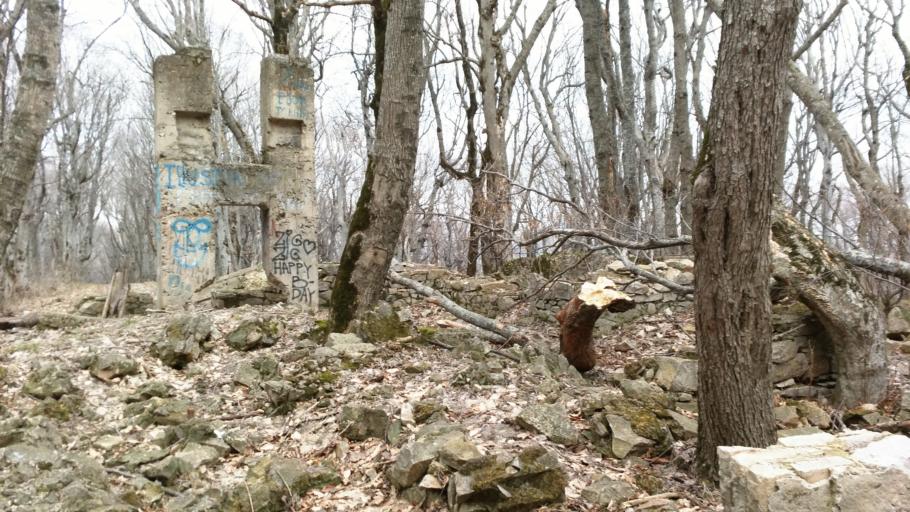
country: RU
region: Stavropol'skiy
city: Zheleznovodsk
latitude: 44.1111
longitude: 43.0260
